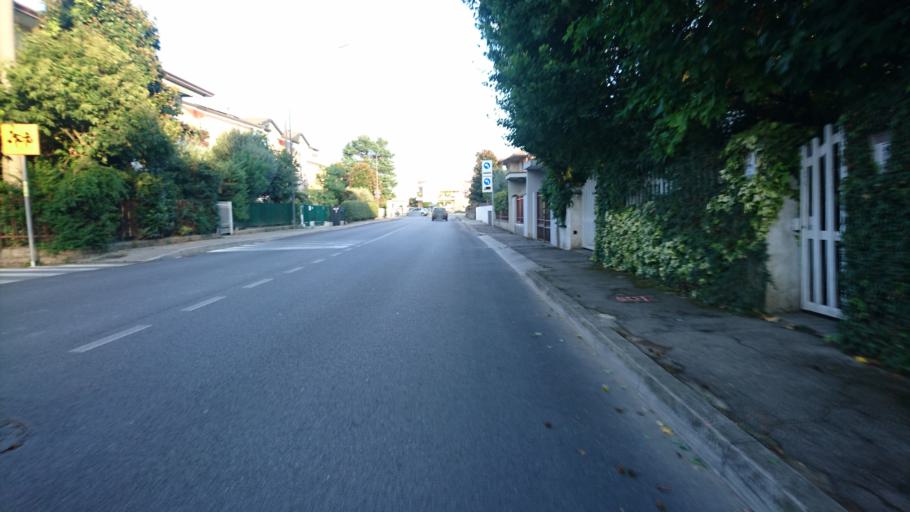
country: IT
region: Veneto
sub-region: Provincia di Padova
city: Montegrotto Terme
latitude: 45.3413
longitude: 11.7751
